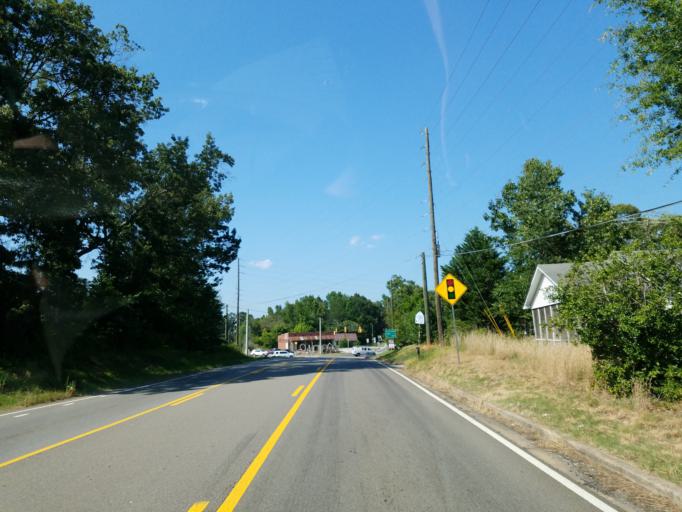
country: US
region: Georgia
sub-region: Fulton County
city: Milton
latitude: 34.2375
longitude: -84.2894
